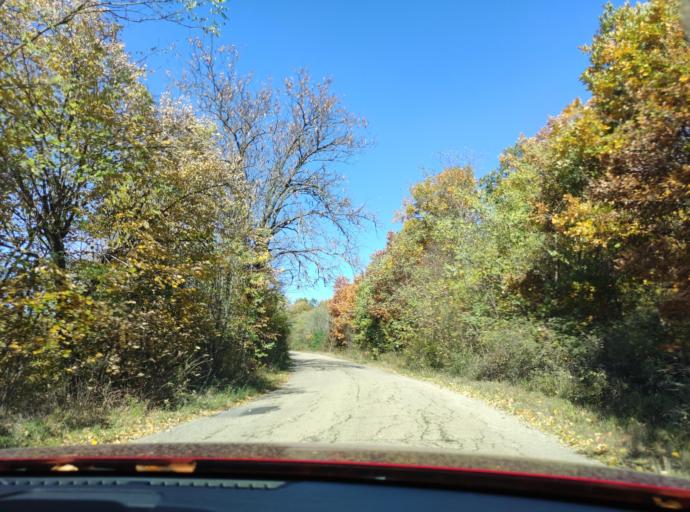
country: BG
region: Montana
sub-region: Obshtina Montana
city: Montana
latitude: 43.4061
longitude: 23.0823
